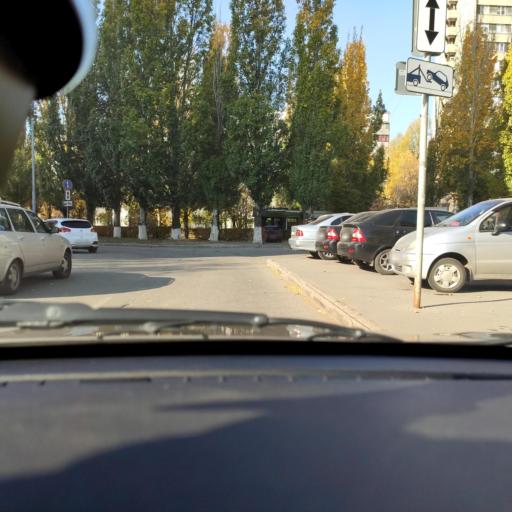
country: RU
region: Samara
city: Tol'yatti
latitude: 53.5338
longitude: 49.3107
